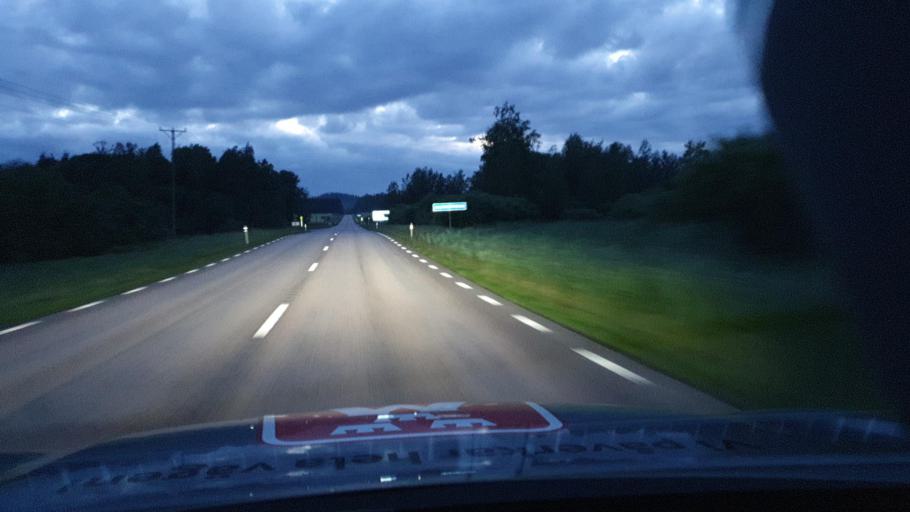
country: SE
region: OErebro
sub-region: Karlskoga Kommun
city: Karlskoga
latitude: 59.4378
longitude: 14.4075
